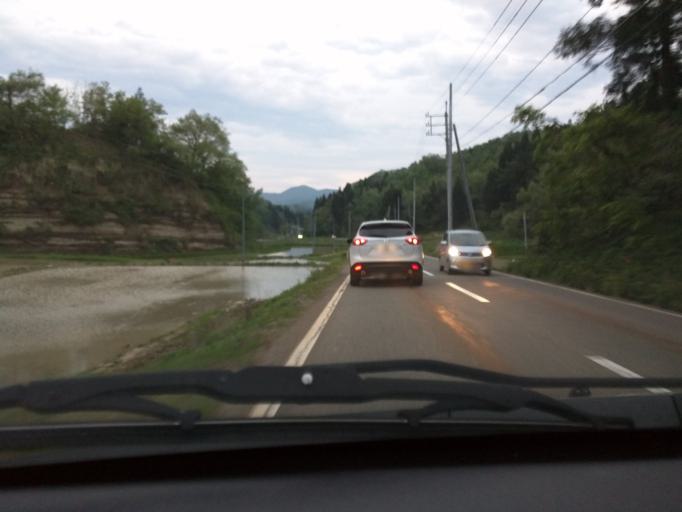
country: JP
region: Niigata
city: Ojiya
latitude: 37.3188
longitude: 138.7298
